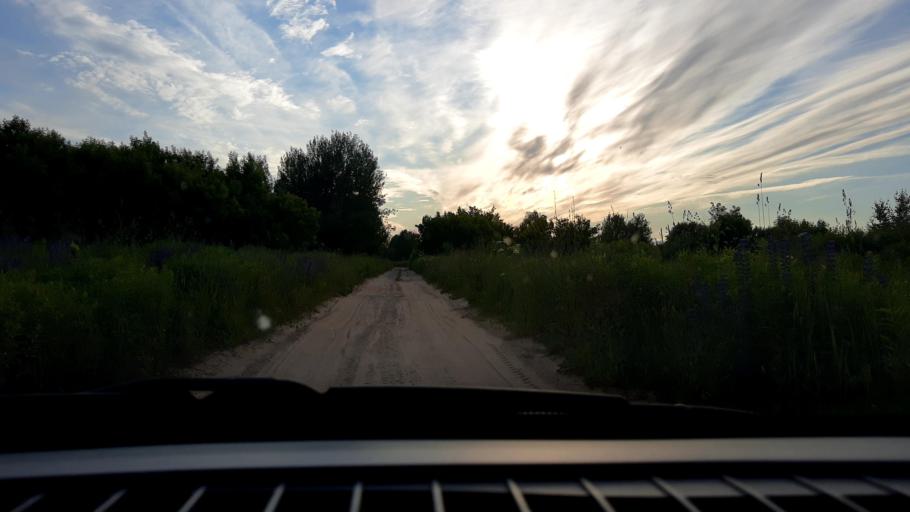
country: RU
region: Nizjnij Novgorod
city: Kstovo
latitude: 56.2653
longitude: 44.3070
